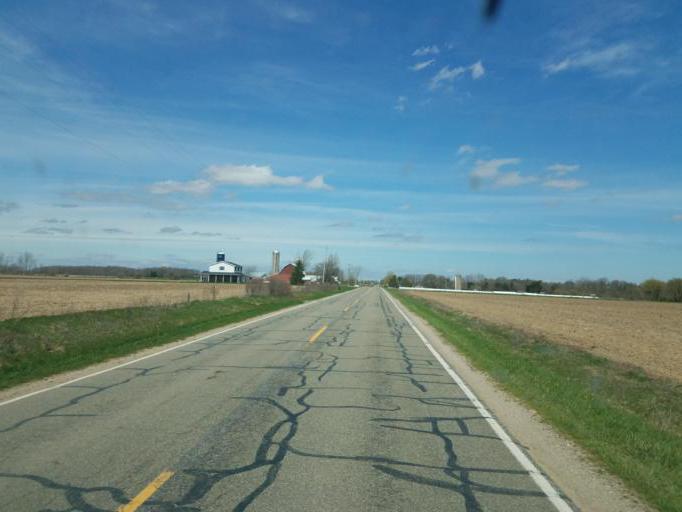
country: US
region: Michigan
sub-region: Isabella County
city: Mount Pleasant
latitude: 43.6810
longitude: -84.7078
